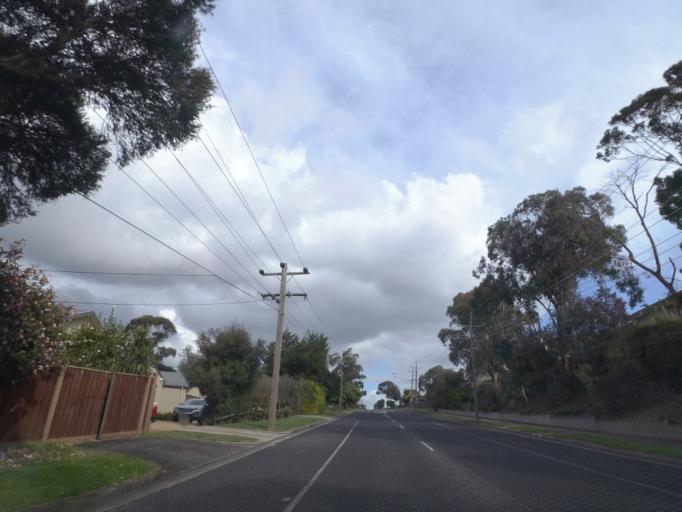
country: AU
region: Victoria
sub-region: Knox
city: Wantirna
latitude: -37.8358
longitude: 145.2134
